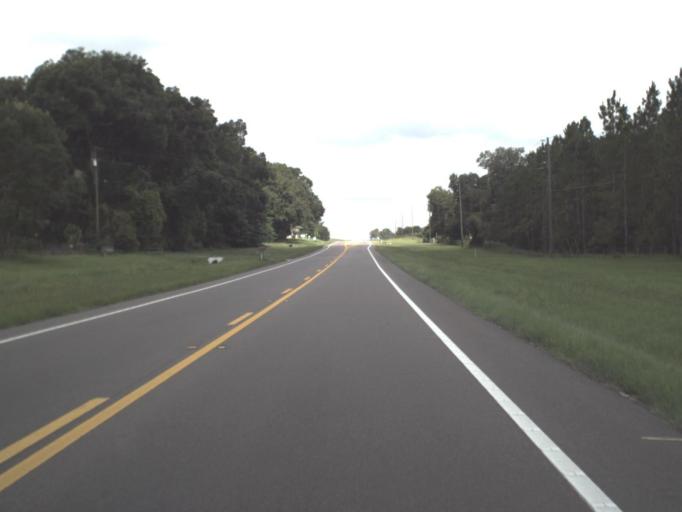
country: US
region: Florida
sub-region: Pasco County
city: Zephyrhills North
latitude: 28.2905
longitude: -82.1316
